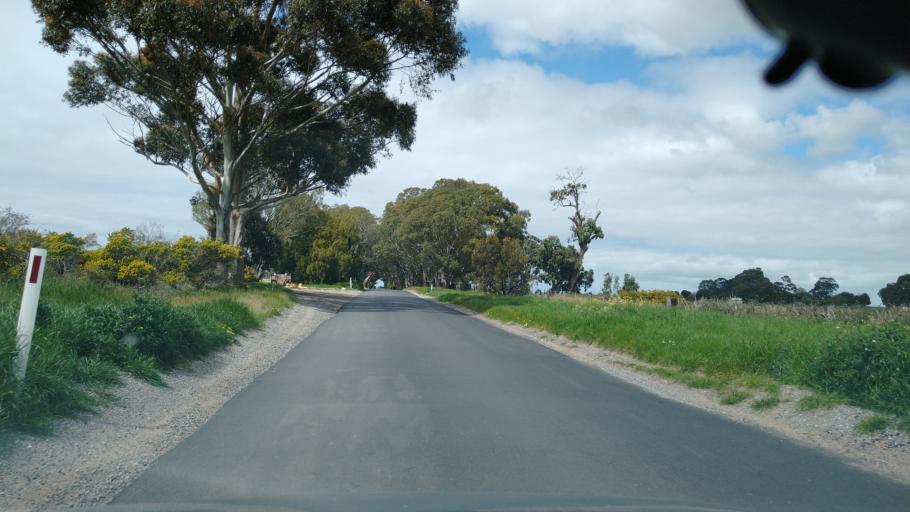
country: AU
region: Victoria
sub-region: Casey
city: Lynbrook
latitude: -38.0619
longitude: 145.2346
